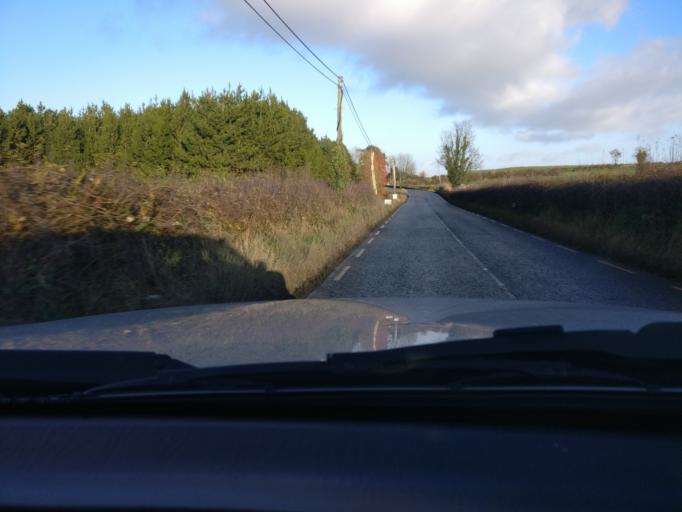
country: IE
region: Ulster
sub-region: An Cabhan
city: Mullagh
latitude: 53.7223
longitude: -6.9982
